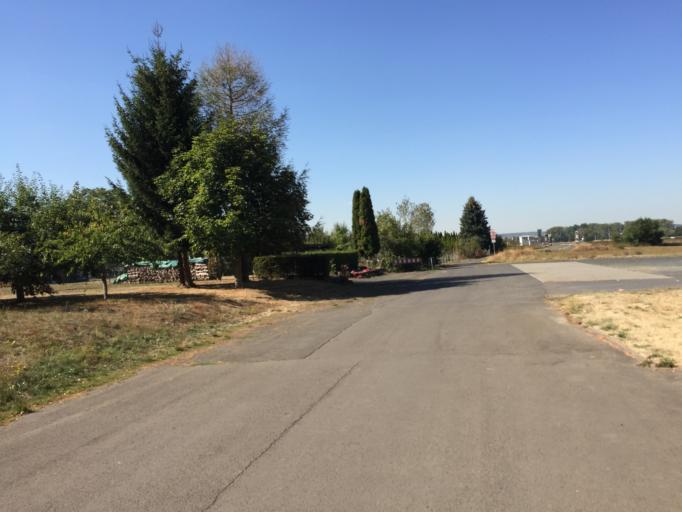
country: DE
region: Hesse
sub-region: Regierungsbezirk Giessen
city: Hungen
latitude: 50.4413
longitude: 8.9206
